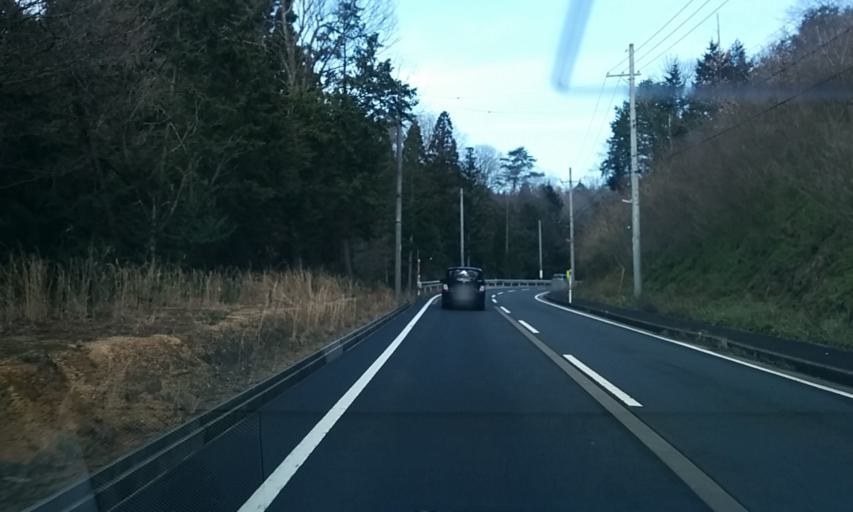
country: JP
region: Kyoto
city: Miyazu
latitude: 35.5798
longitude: 135.1190
